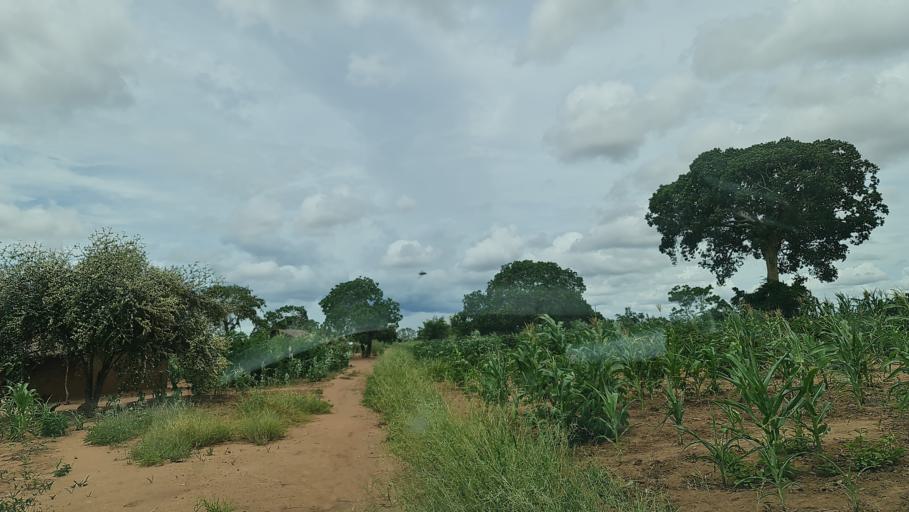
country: MZ
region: Nampula
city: Nacala
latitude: -14.7807
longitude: 39.9859
